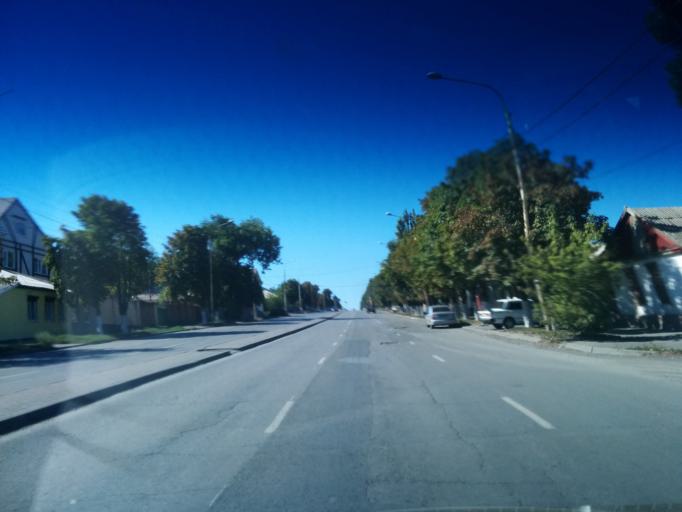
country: RU
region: Rostov
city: Shakhty
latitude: 47.6995
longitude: 40.2350
